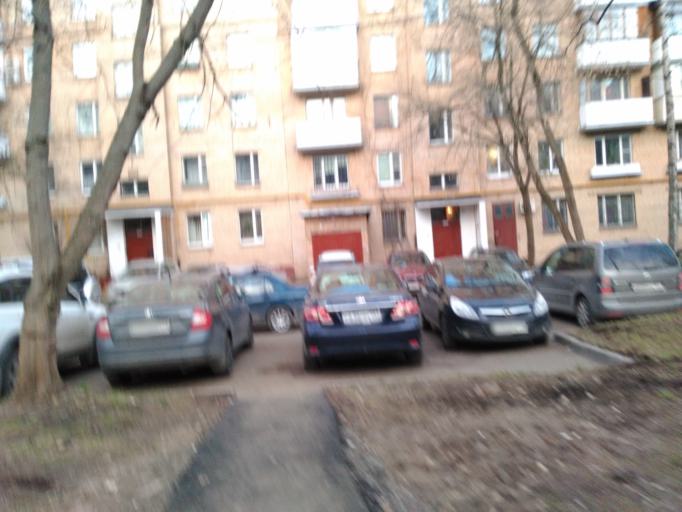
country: RU
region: Moskovskaya
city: Khoroshevo-Mnevniki
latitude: 55.7880
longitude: 37.4639
